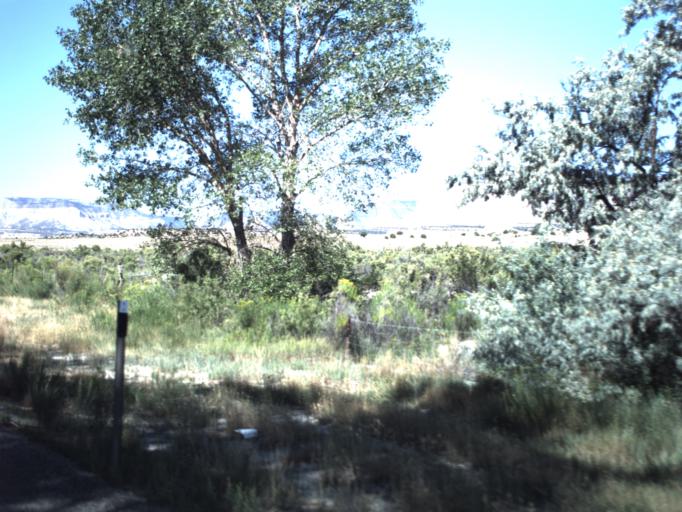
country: US
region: Utah
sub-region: Emery County
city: Ferron
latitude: 38.9197
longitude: -111.2612
